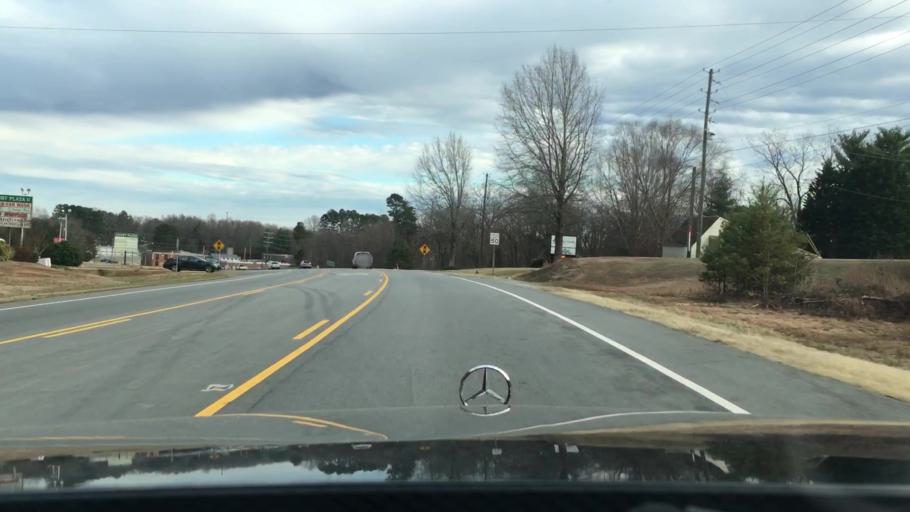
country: US
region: North Carolina
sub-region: Caswell County
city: Yanceyville
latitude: 36.4085
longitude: -79.3400
